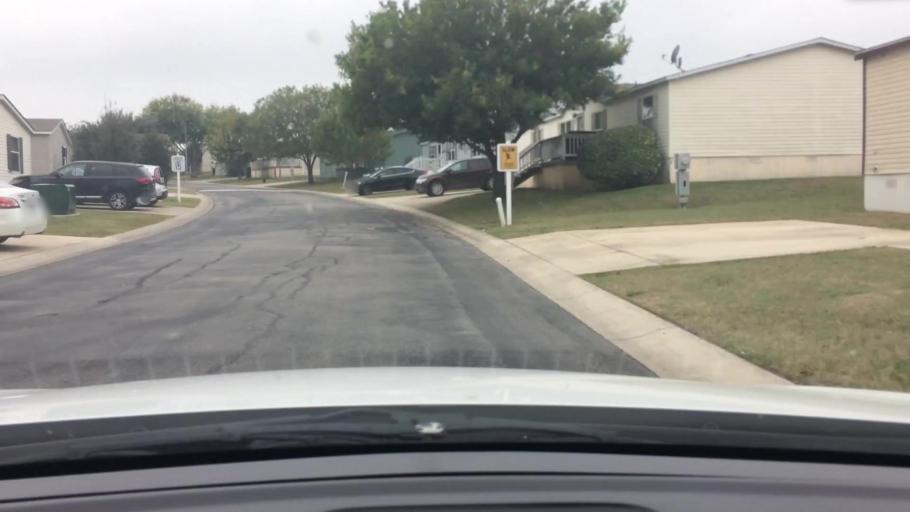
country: US
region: Texas
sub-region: Bexar County
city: Converse
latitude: 29.5247
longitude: -98.3378
